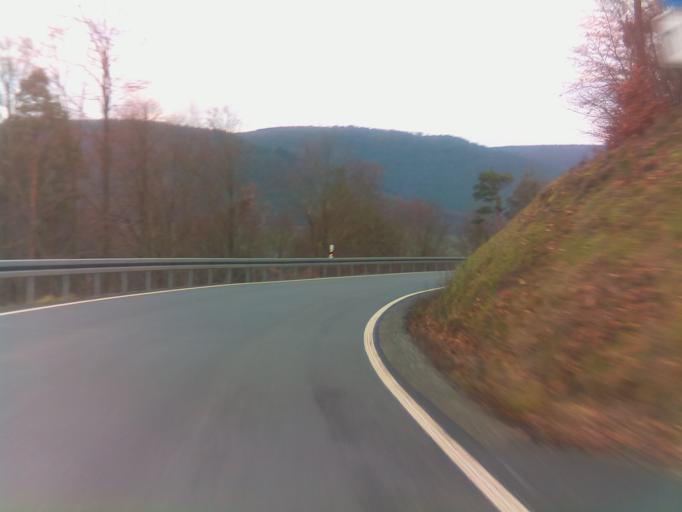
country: DE
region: Bavaria
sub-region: Regierungsbezirk Unterfranken
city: Miltenberg
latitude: 49.6979
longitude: 9.2832
